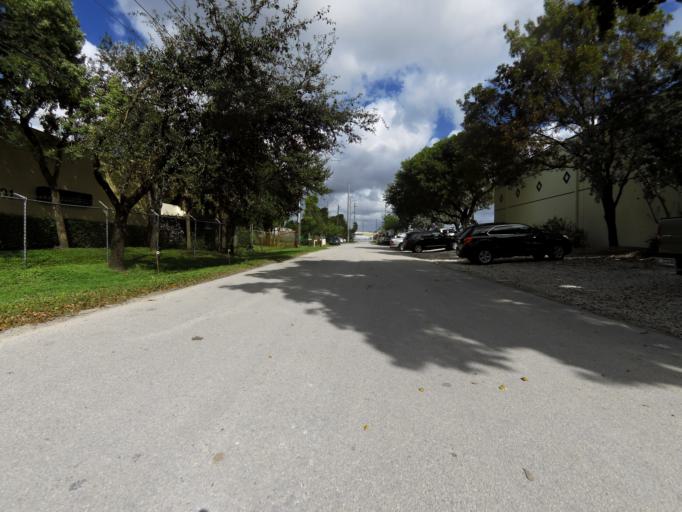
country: US
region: Florida
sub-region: Broward County
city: Broadview Park
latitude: 26.0927
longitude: -80.2356
